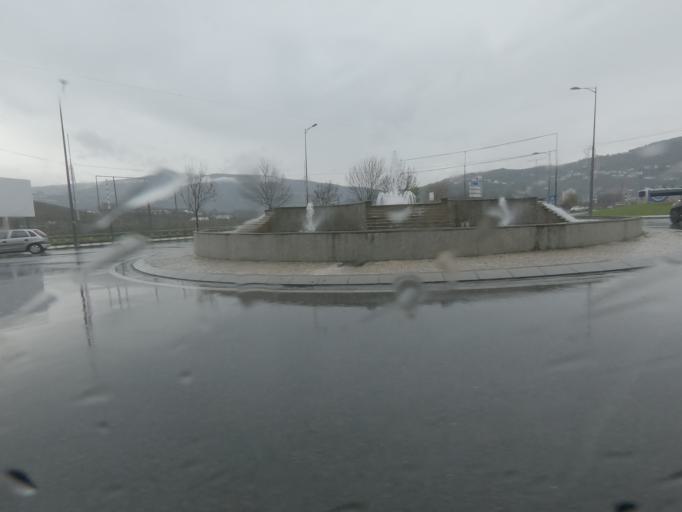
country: PT
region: Vila Real
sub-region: Peso da Regua
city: Peso da Regua
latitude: 41.1623
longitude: -7.7918
